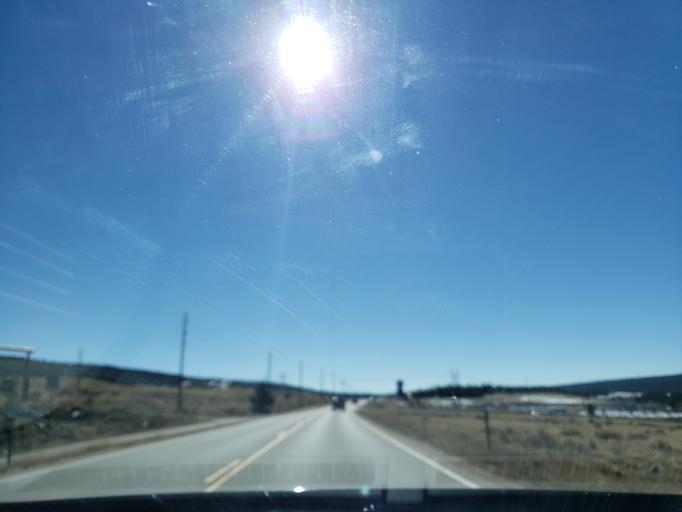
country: US
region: Colorado
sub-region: Park County
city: Fairplay
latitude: 39.2714
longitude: -106.0483
